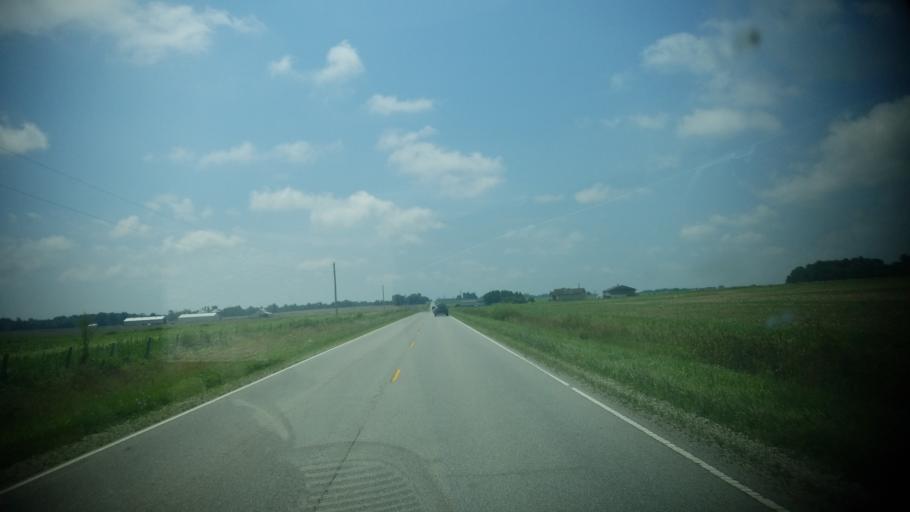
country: US
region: Illinois
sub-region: Wayne County
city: Fairfield
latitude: 38.4508
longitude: -88.3491
